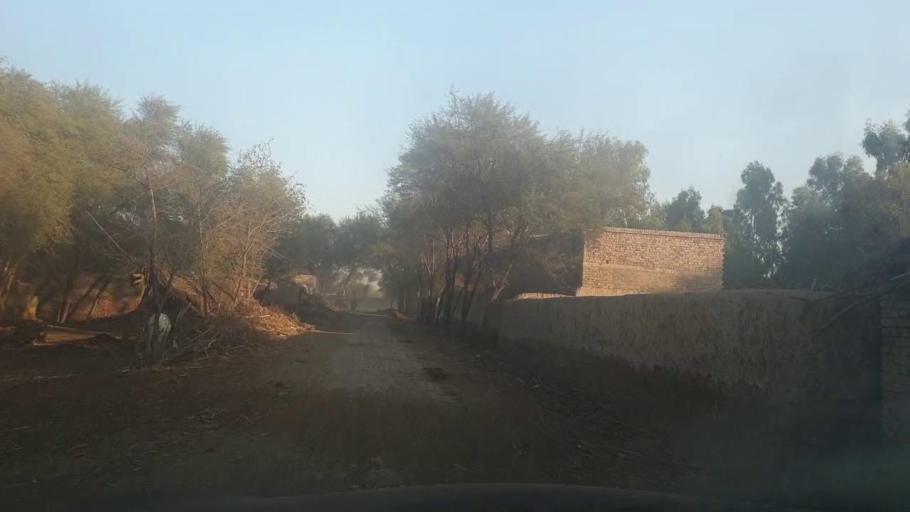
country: PK
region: Sindh
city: Mirpur Mathelo
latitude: 28.1724
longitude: 69.5763
